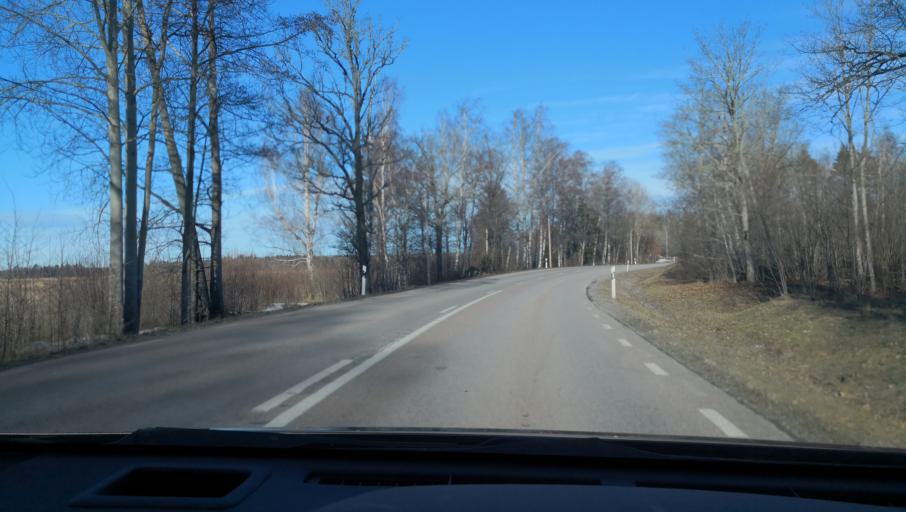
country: SE
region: Uppsala
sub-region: Osthammars Kommun
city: Osterbybruk
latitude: 60.1761
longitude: 17.8498
